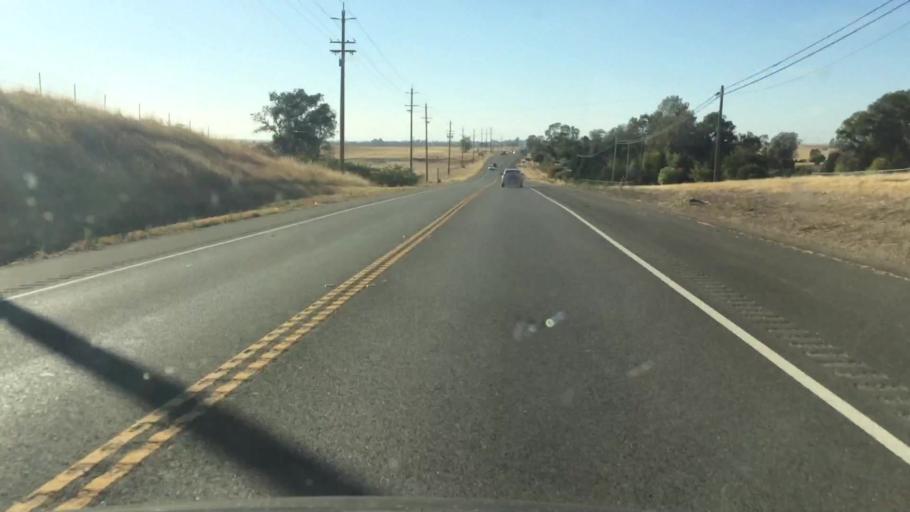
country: US
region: California
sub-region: Sacramento County
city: Wilton
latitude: 38.5005
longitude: -121.2162
